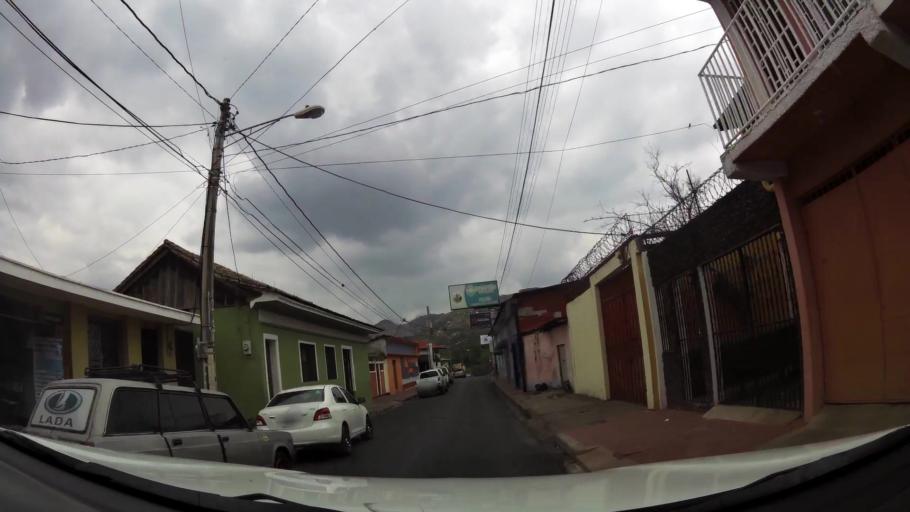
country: NI
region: Matagalpa
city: Matagalpa
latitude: 12.9237
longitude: -85.9191
